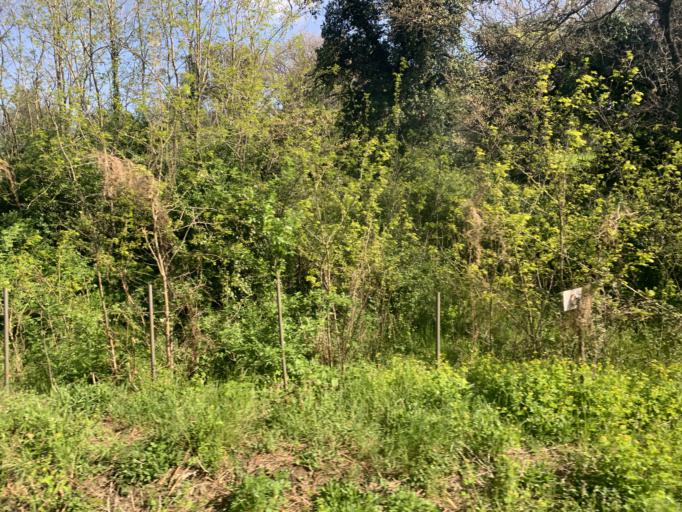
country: IT
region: Latium
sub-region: Citta metropolitana di Roma Capitale
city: Marino
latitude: 41.7780
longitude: 12.6370
